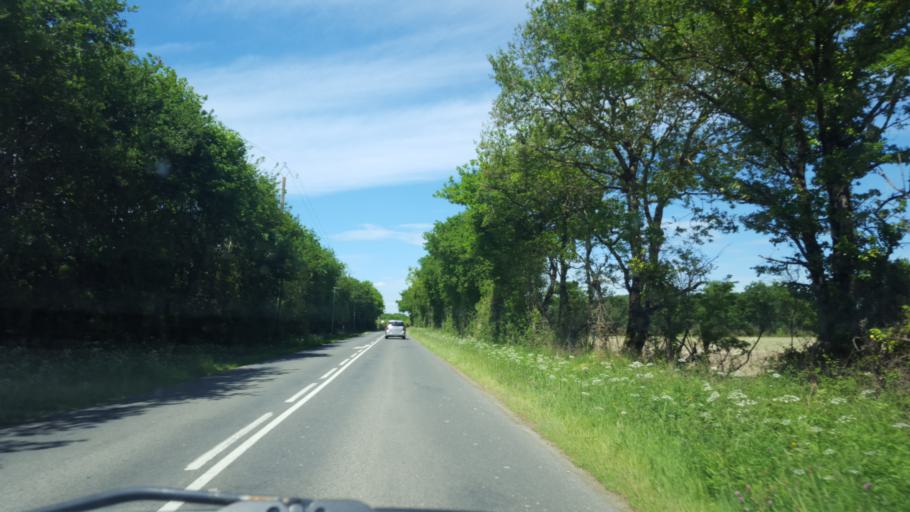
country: FR
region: Pays de la Loire
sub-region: Departement de la Loire-Atlantique
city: Saint-Philbert-de-Grand-Lieu
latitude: 47.0004
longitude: -1.6627
